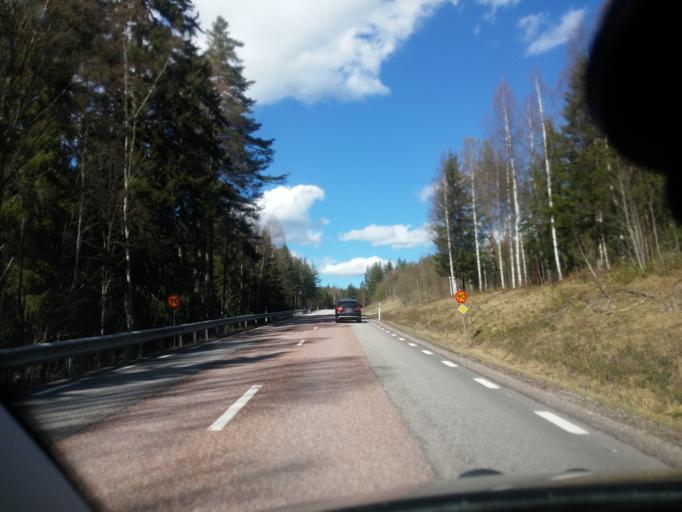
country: SE
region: Dalarna
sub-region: Faluns Kommun
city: Svardsjo
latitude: 60.7287
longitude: 15.7665
